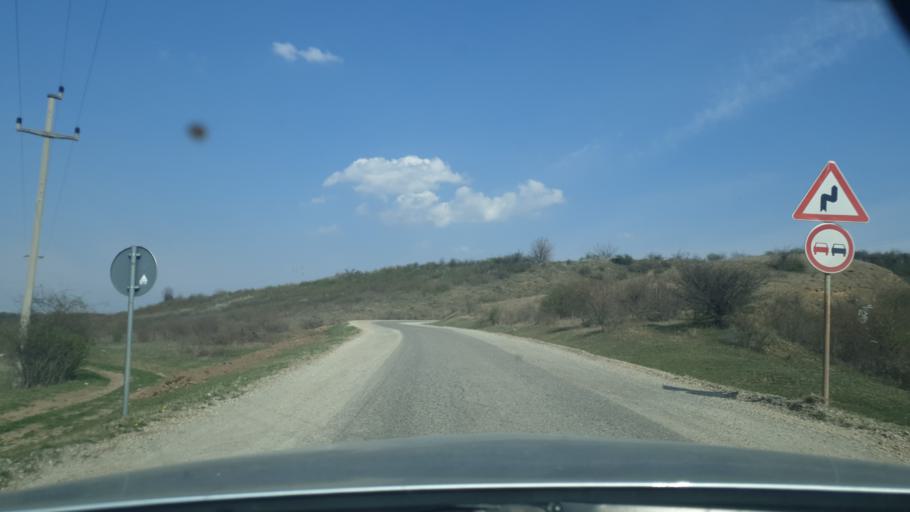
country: RS
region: Autonomna Pokrajina Vojvodina
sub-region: Sremski Okrug
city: Irig
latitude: 45.1062
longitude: 19.9151
